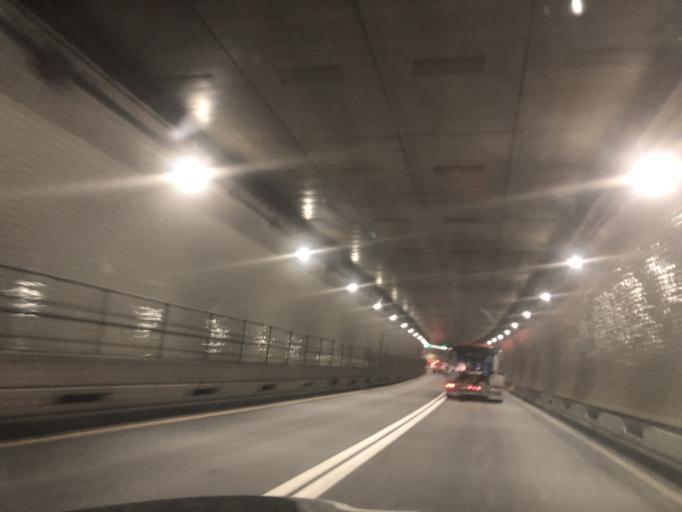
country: US
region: Maryland
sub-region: City of Baltimore
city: Baltimore
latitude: 39.2608
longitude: -76.5824
